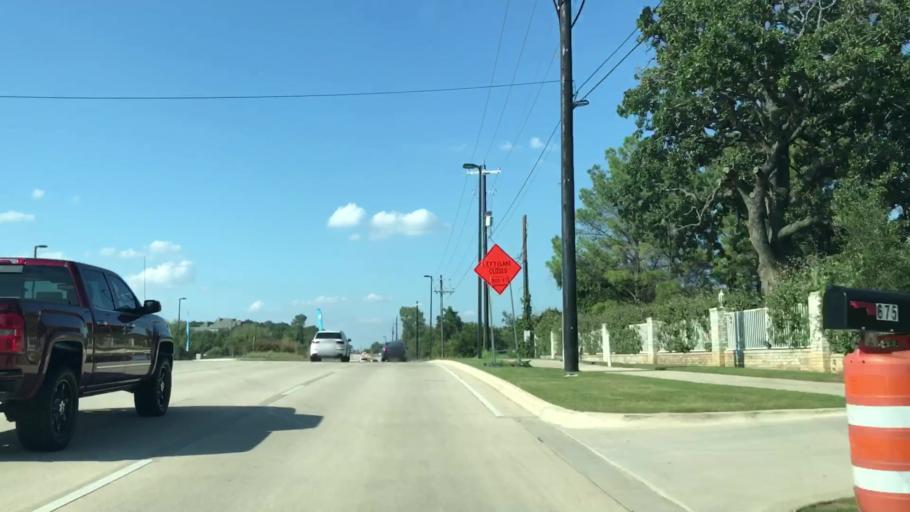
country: US
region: Texas
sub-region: Denton County
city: Trophy Club
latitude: 32.9485
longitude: -97.1857
